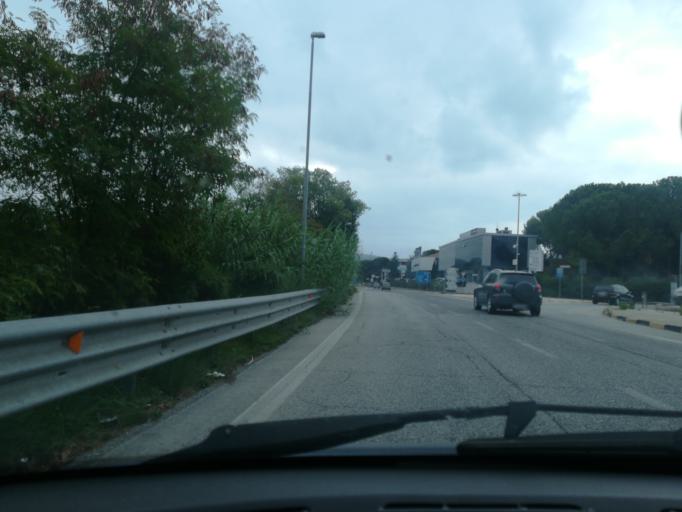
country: IT
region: The Marches
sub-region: Provincia di Macerata
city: Zona Industriale
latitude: 43.2664
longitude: 13.4881
